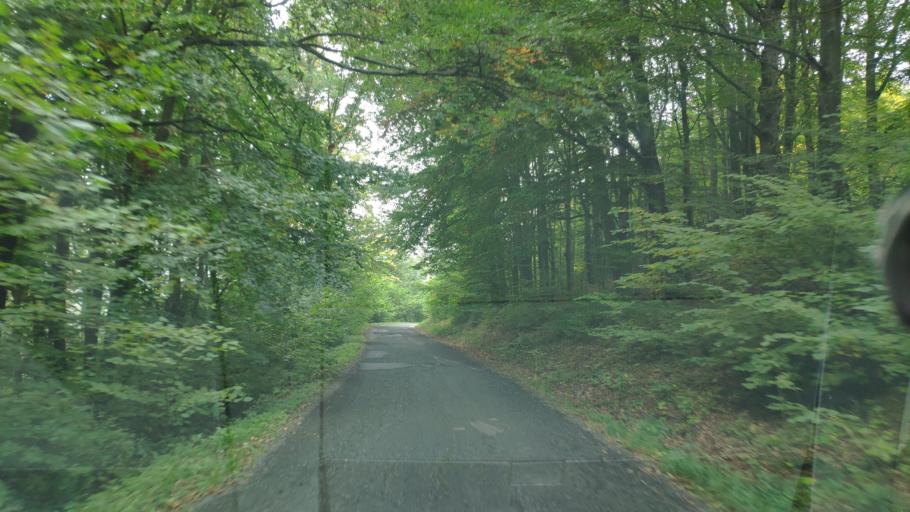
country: SK
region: Presovsky
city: Giraltovce
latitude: 48.9155
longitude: 21.4595
